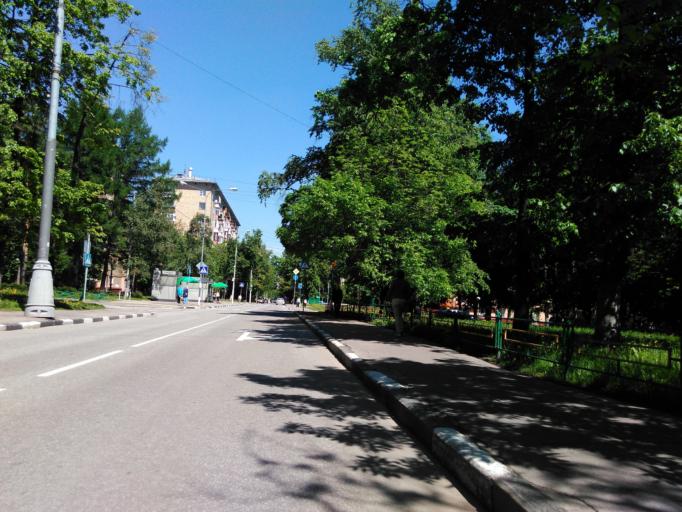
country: RU
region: Moskovskaya
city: Semenovskoye
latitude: 55.6921
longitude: 37.5479
